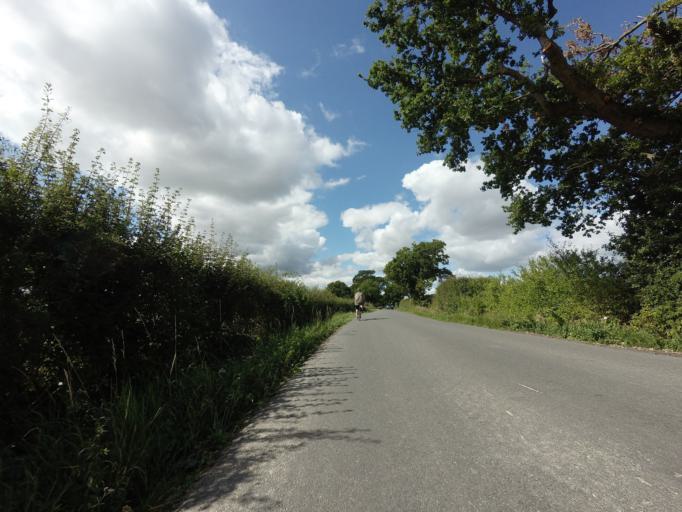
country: GB
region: England
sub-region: Kent
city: Staplehurst
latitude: 51.1522
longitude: 0.5366
